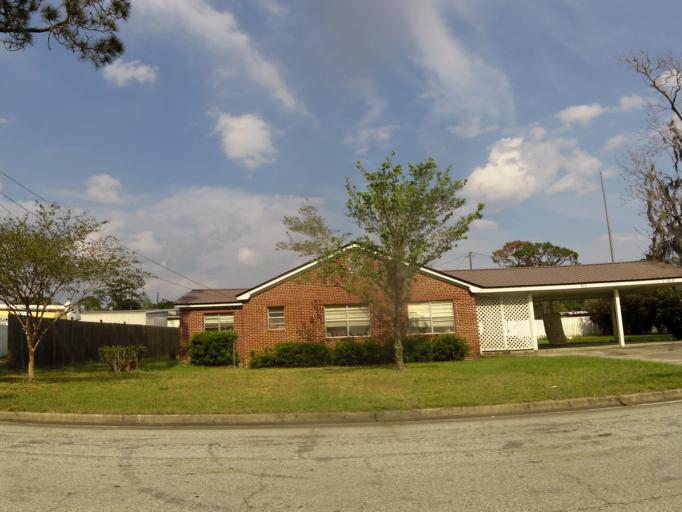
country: US
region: Georgia
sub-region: Charlton County
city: Folkston
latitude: 30.8283
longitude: -82.0061
